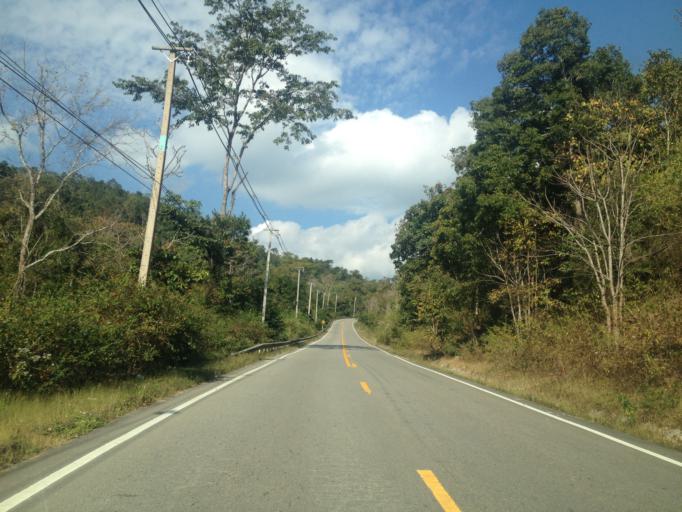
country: TH
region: Mae Hong Son
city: Ban Huai I Huak
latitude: 18.1369
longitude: 98.1757
